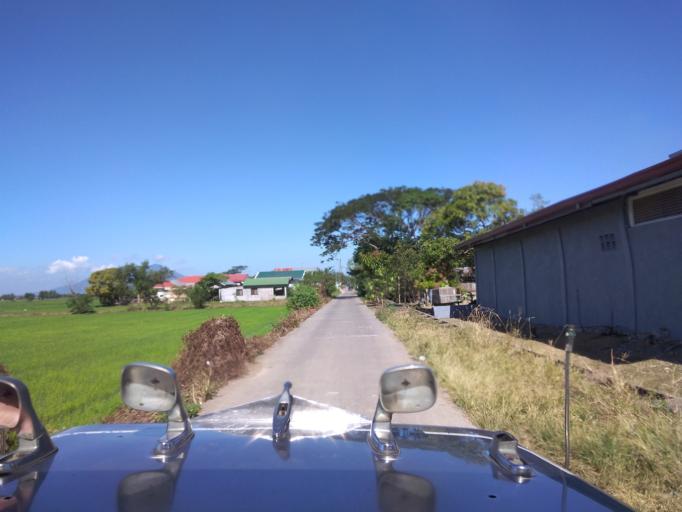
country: PH
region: Central Luzon
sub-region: Province of Pampanga
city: Salapungan
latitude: 15.1530
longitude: 120.9227
